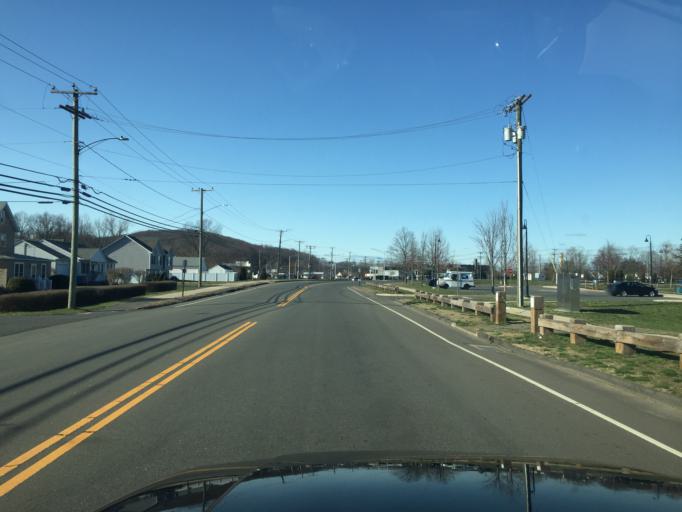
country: US
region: Connecticut
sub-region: Hartford County
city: Bristol
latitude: 41.6632
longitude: -72.9224
